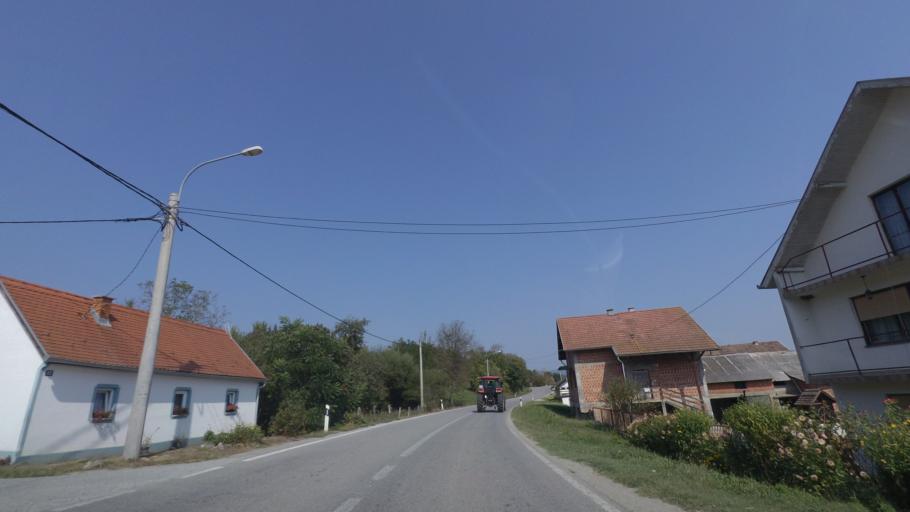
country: HR
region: Brodsko-Posavska
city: Resetari
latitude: 45.3743
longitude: 17.5173
